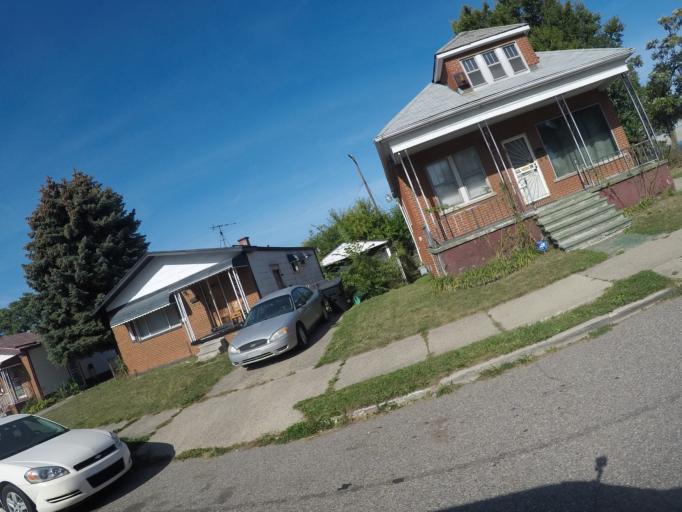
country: US
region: Michigan
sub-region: Wayne County
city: Lincoln Park
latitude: 42.2637
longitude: -83.1644
